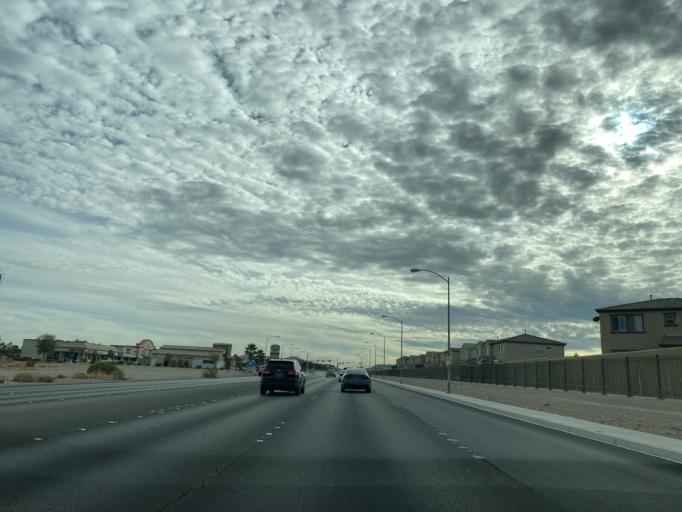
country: US
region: Nevada
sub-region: Clark County
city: Enterprise
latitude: 36.0441
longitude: -115.2791
